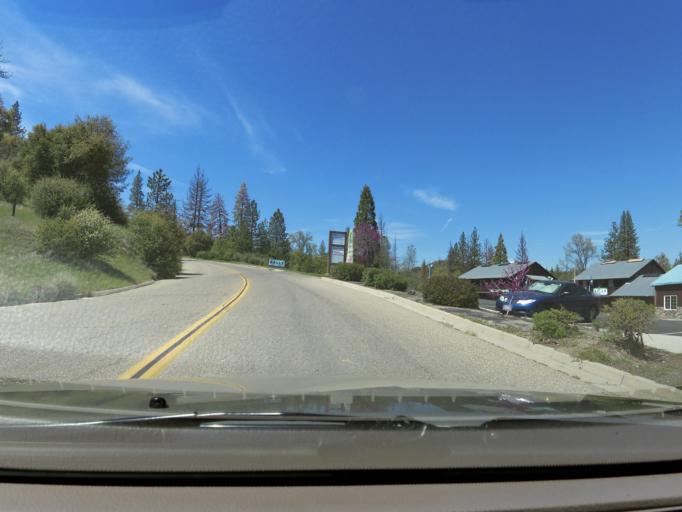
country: US
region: California
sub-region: Fresno County
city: Auberry
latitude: 37.2295
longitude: -119.5098
